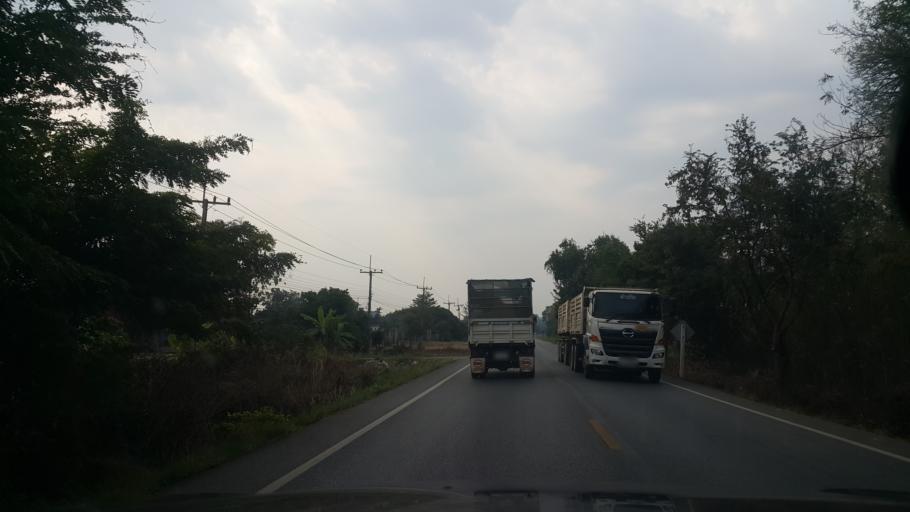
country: TH
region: Sukhothai
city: Si Samrong
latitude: 17.1110
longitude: 99.8893
